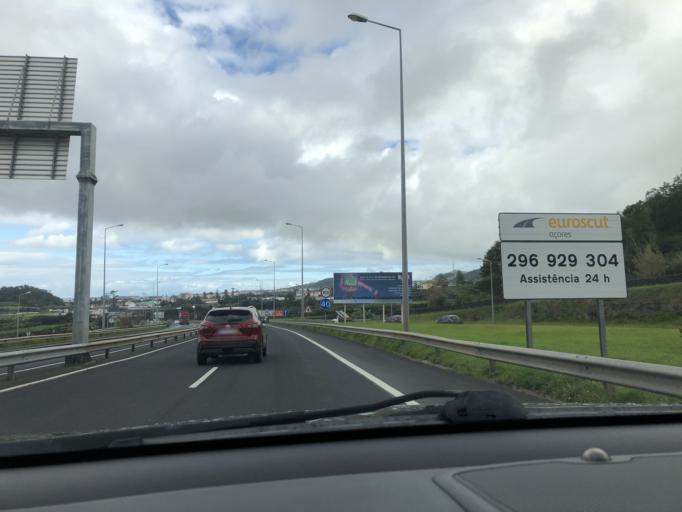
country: PT
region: Azores
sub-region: Ponta Delgada
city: Rosto de Cao
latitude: 37.7588
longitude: -25.6242
